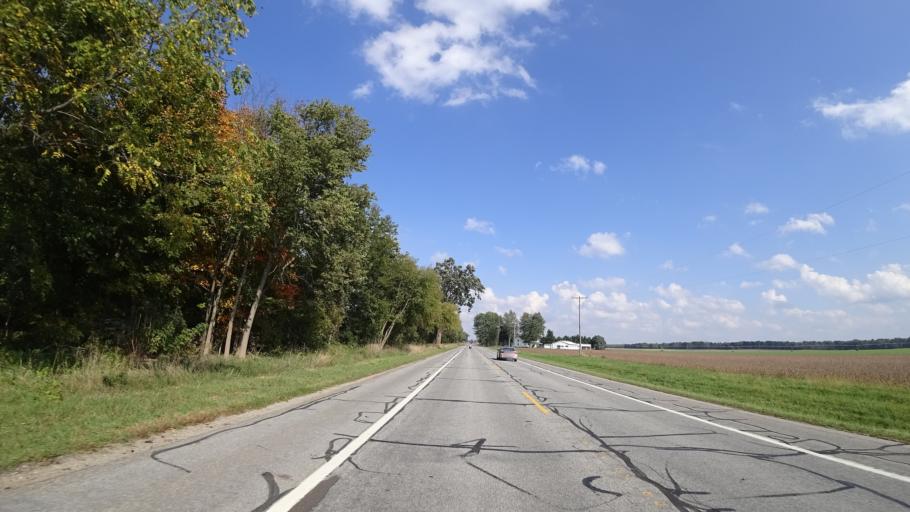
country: US
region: Michigan
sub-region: Saint Joseph County
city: Colon
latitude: 42.0309
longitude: -85.3393
